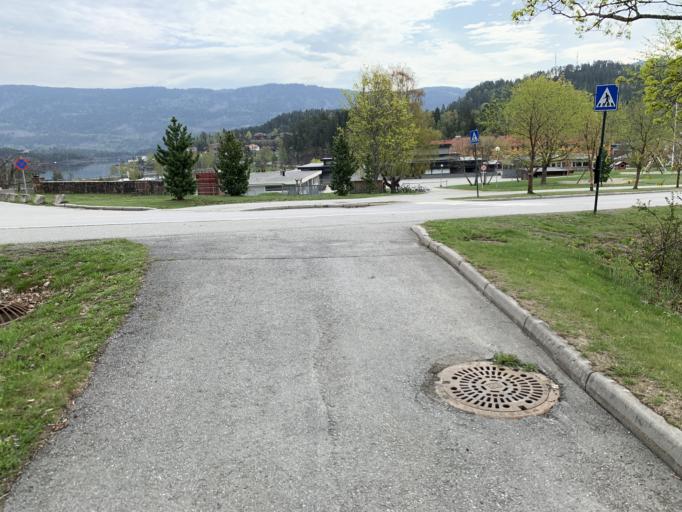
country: NO
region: Buskerud
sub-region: Hole
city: Vik
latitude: 60.0799
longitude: 10.2794
